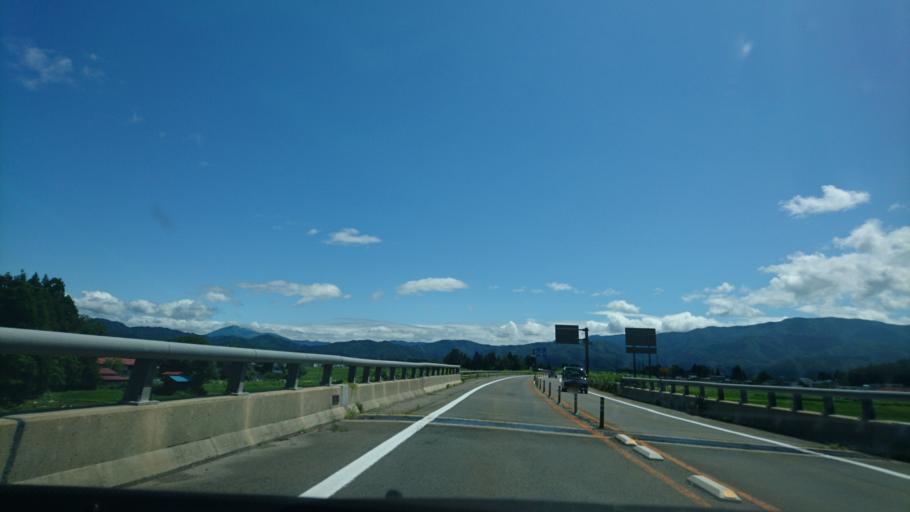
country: JP
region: Akita
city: Kakunodatemachi
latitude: 39.6119
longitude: 140.5626
